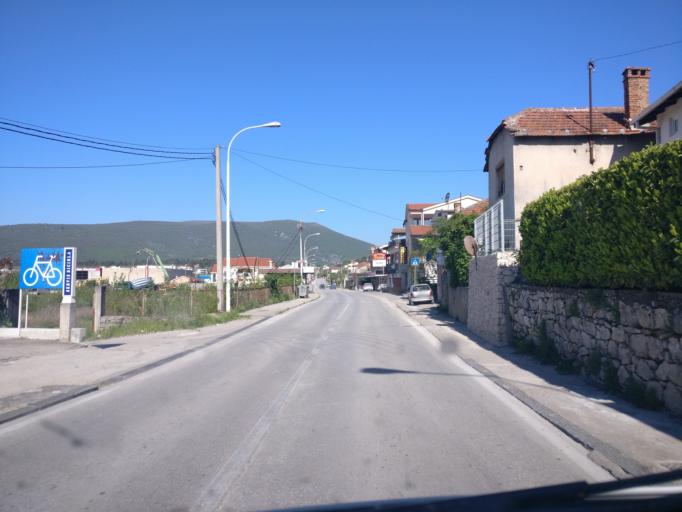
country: BA
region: Federation of Bosnia and Herzegovina
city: Capljina
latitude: 43.1165
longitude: 17.6991
